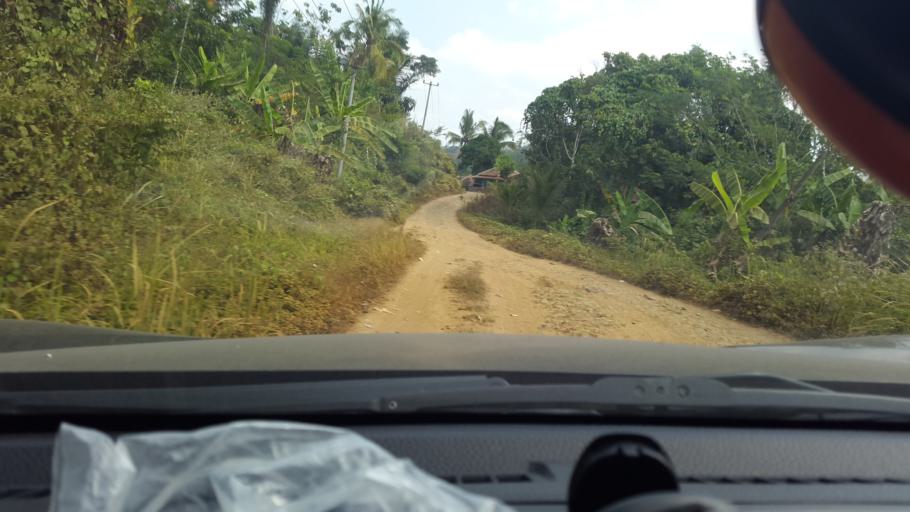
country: ID
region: West Java
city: Buniwangi
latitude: -7.2749
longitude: 106.7835
